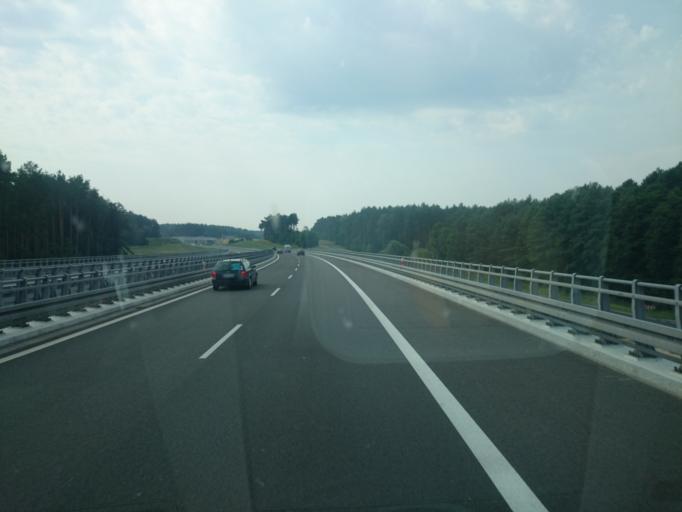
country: PL
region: Lubusz
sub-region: Powiat miedzyrzecki
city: Miedzyrzecz
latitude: 52.4108
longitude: 15.5426
